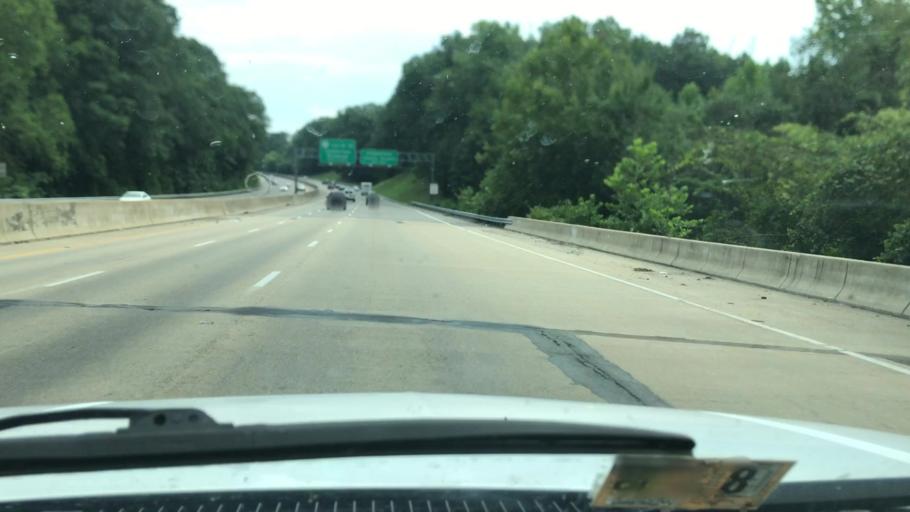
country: US
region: Virginia
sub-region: Chesterfield County
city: Bensley
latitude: 37.4577
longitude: -77.4956
